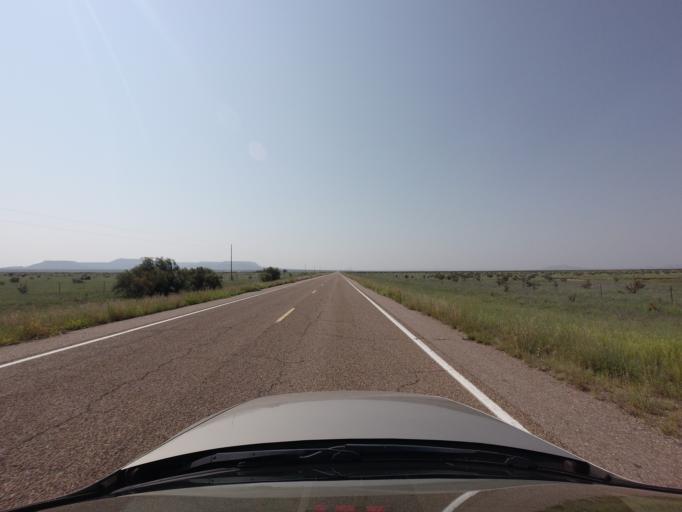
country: US
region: New Mexico
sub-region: Quay County
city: Tucumcari
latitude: 35.0553
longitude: -103.7376
